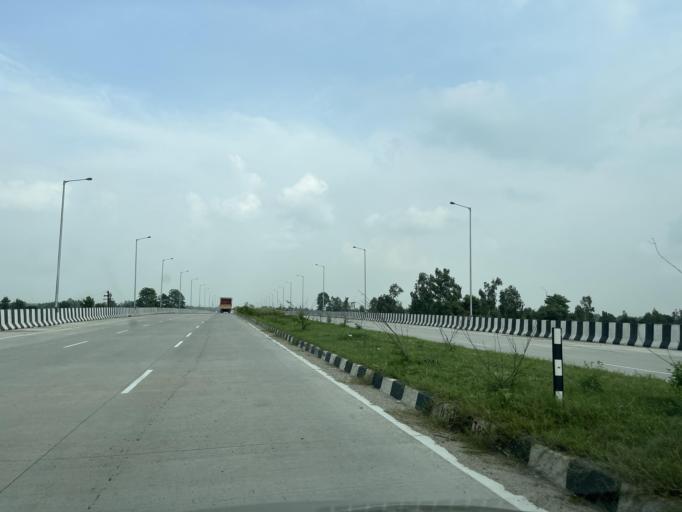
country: IN
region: Uttarakhand
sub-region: Udham Singh Nagar
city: Bazpur
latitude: 29.1488
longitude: 79.0562
